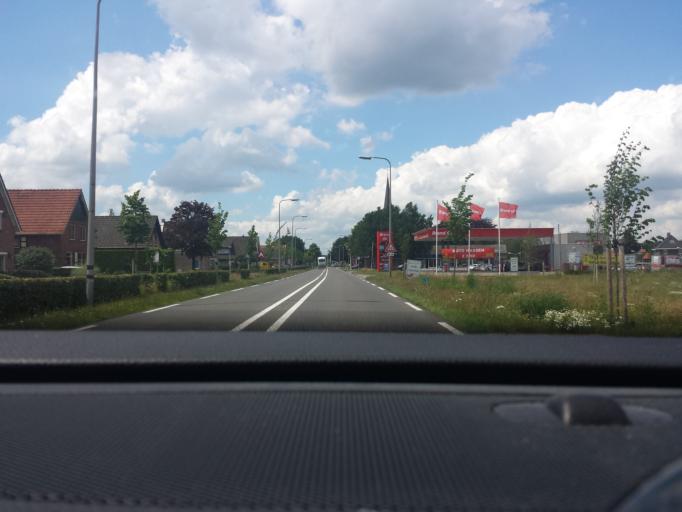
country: NL
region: Overijssel
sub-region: Gemeente Haaksbergen
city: Haaksbergen
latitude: 52.1756
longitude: 6.7035
